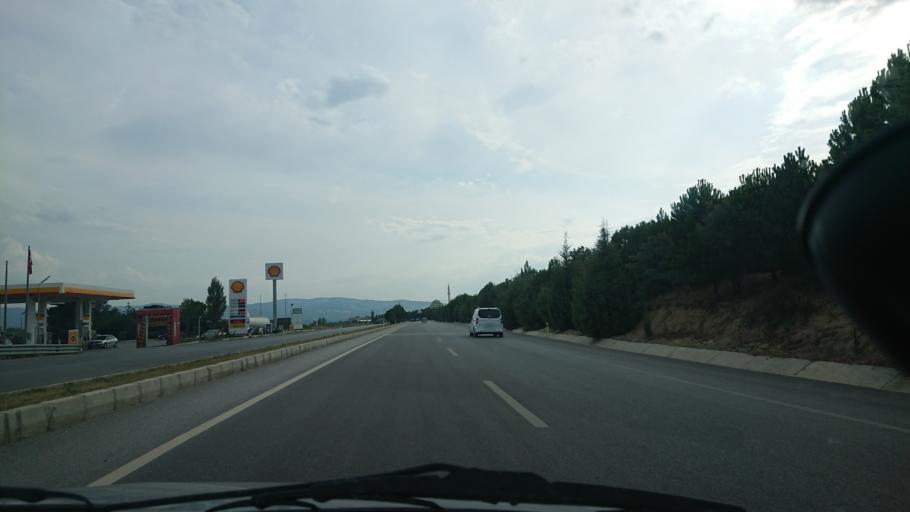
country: TR
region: Kuetahya
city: Gediz
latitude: 39.0095
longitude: 29.4079
